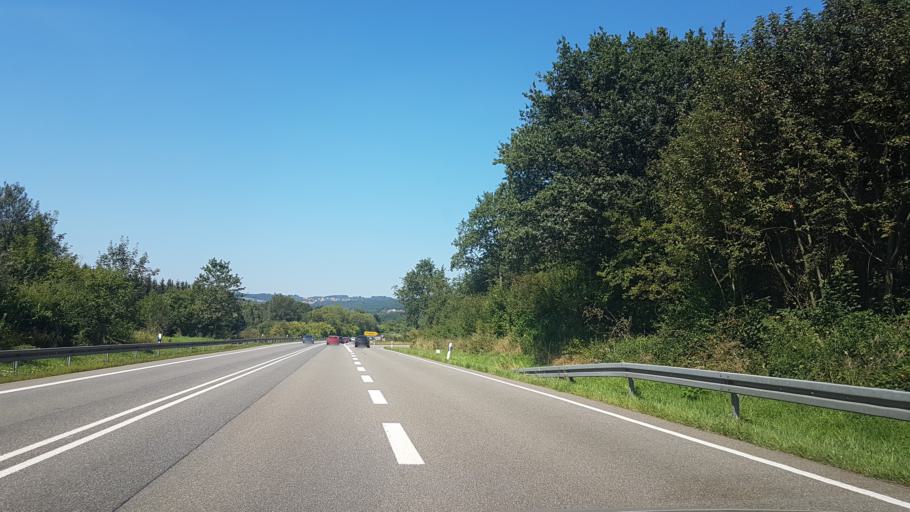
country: DE
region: Saarland
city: Namborn
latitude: 49.5009
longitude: 7.1490
